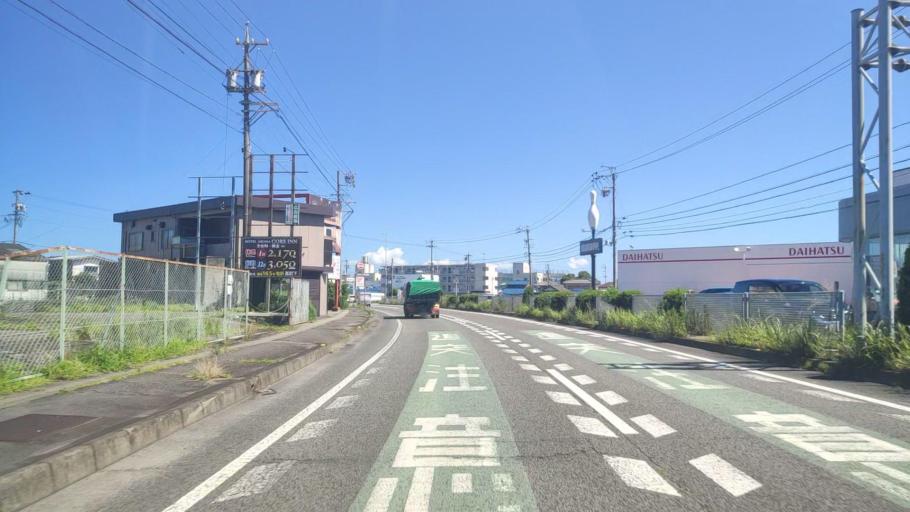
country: JP
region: Mie
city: Tsu-shi
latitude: 34.6916
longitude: 136.5110
